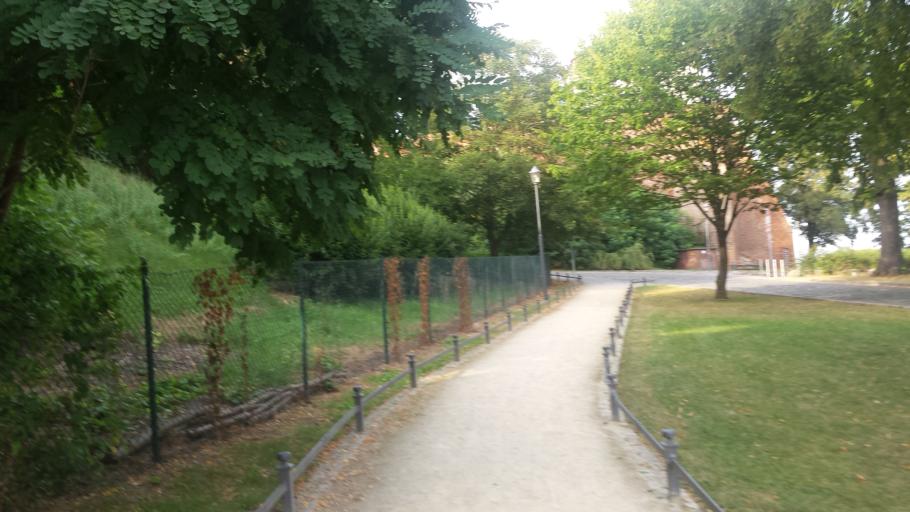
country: DE
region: Saxony-Anhalt
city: Tangermunde
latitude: 52.5421
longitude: 11.9768
